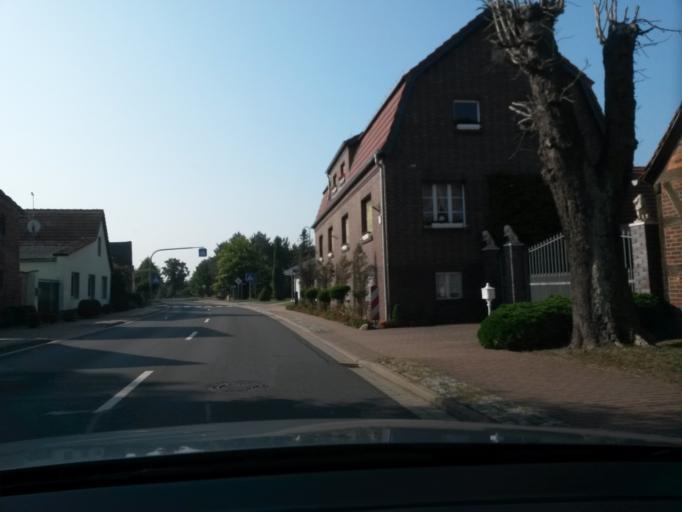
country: DE
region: Saxony-Anhalt
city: Tangermunde
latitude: 52.5098
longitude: 11.9264
